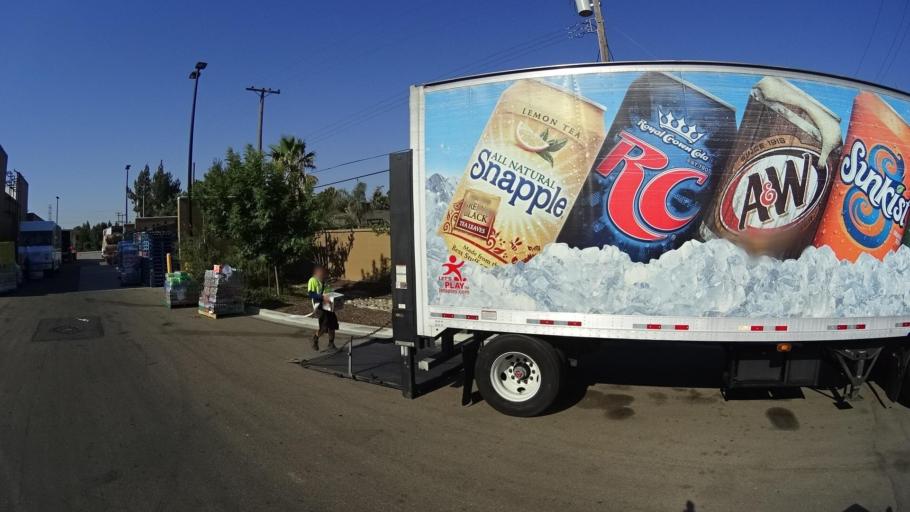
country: US
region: California
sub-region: Fresno County
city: Fresno
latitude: 36.7794
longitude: -119.7566
